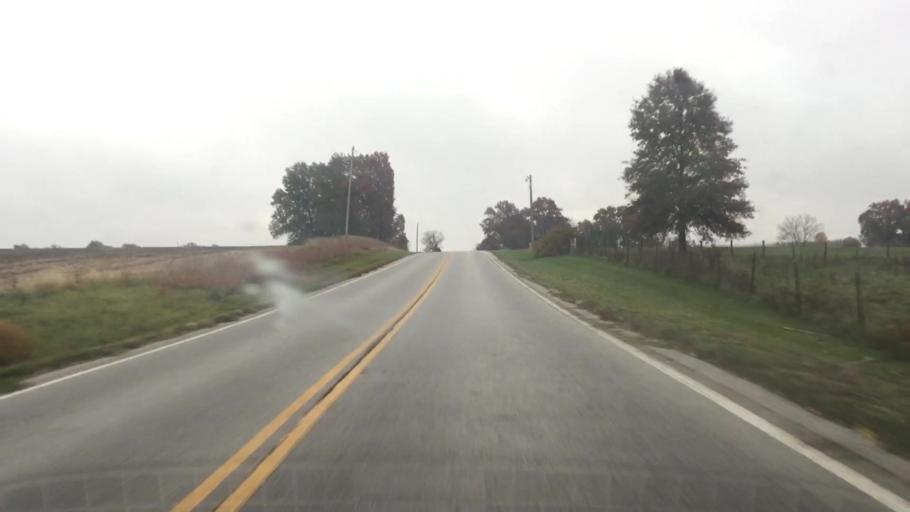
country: US
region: Missouri
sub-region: Boone County
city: Columbia
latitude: 38.9186
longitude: -92.1858
